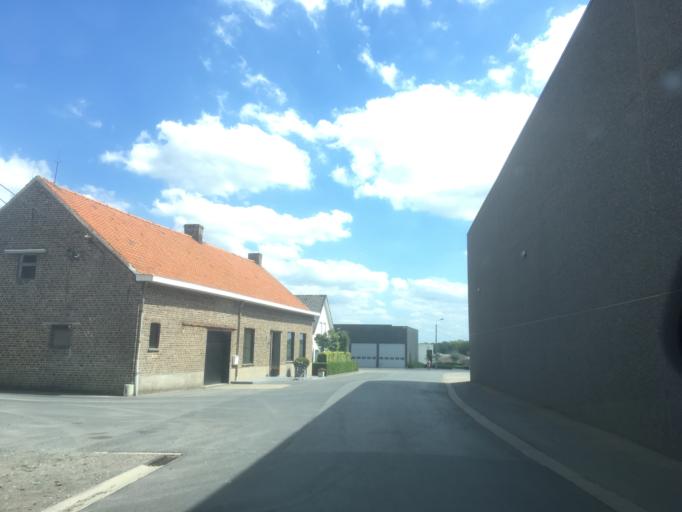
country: BE
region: Flanders
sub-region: Provincie West-Vlaanderen
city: Staden
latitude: 50.9434
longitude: 3.0164
